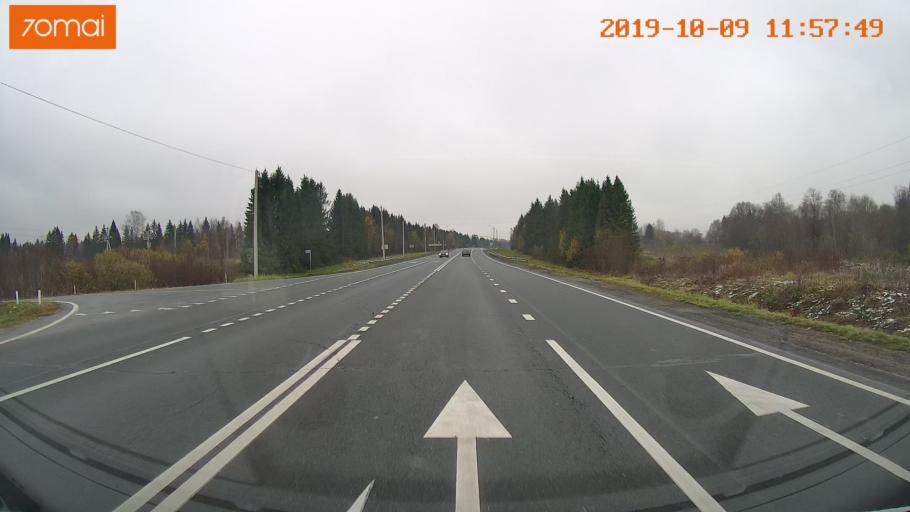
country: RU
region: Vologda
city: Gryazovets
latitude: 58.7270
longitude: 40.2948
